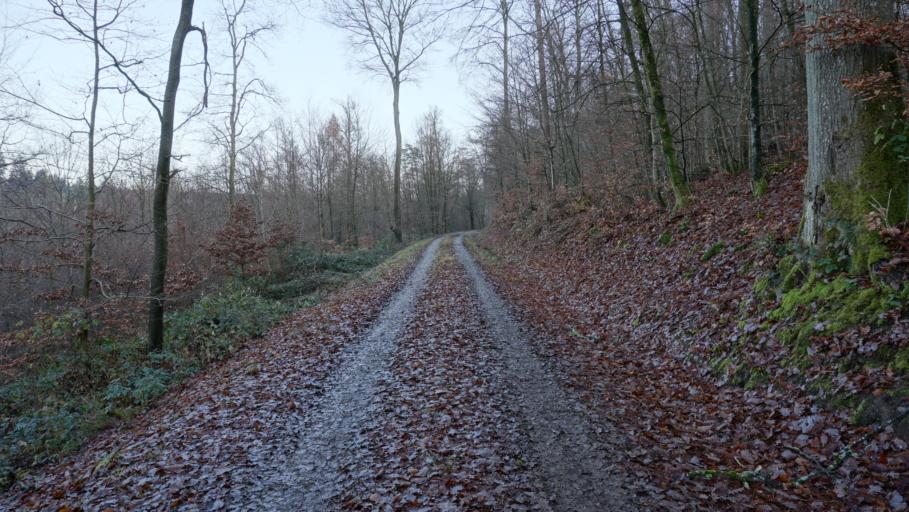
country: DE
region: Baden-Wuerttemberg
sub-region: Karlsruhe Region
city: Zwingenberg
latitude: 49.4095
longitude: 9.0528
